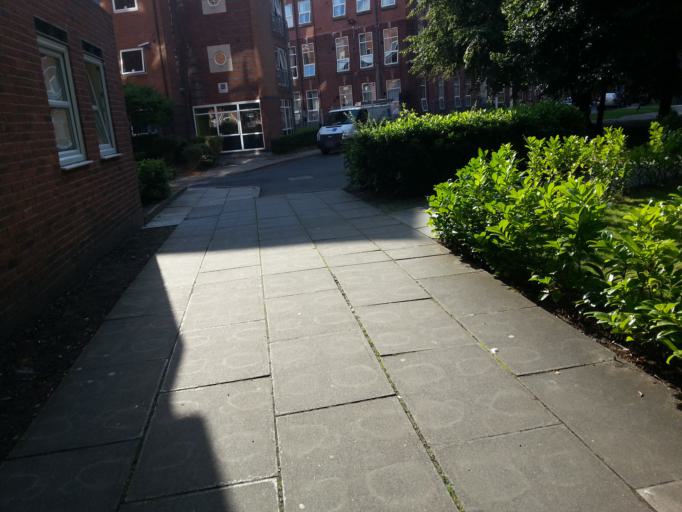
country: GB
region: England
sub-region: Liverpool
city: Liverpool
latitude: 53.4025
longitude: -2.9670
